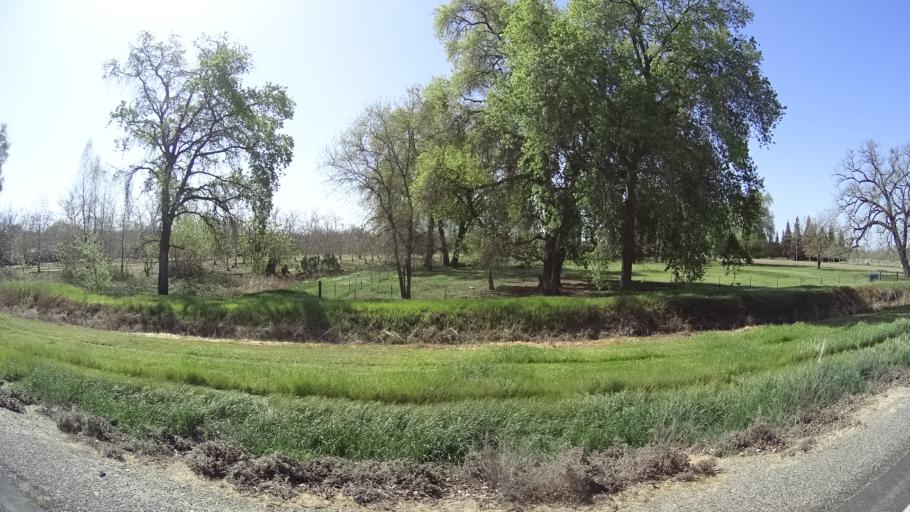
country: US
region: California
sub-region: Glenn County
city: Willows
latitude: 39.4574
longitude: -122.0212
